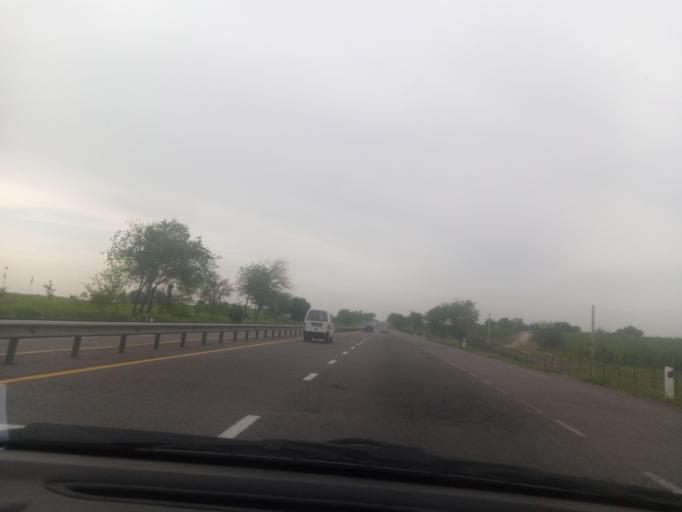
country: UZ
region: Toshkent
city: Tuytepa
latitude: 41.1155
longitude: 69.4453
